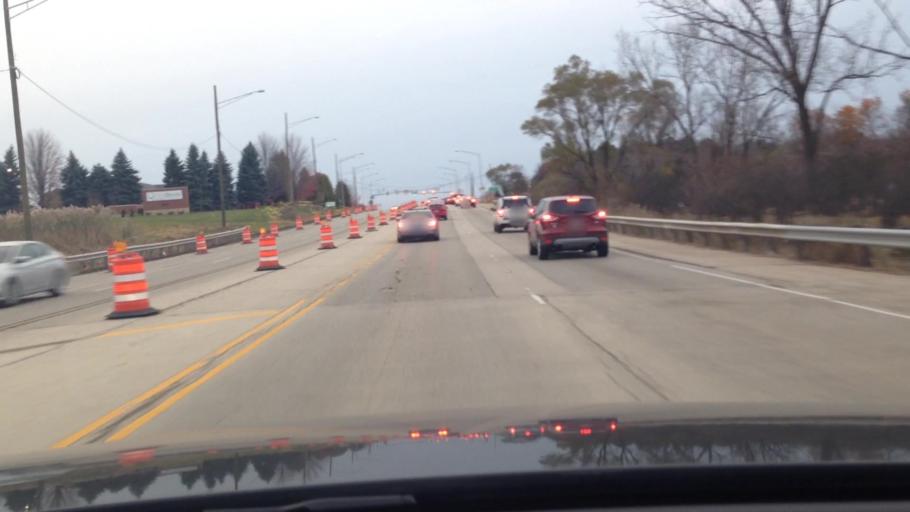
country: US
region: Illinois
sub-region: McHenry County
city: Lake in the Hills
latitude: 42.1651
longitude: -88.3354
